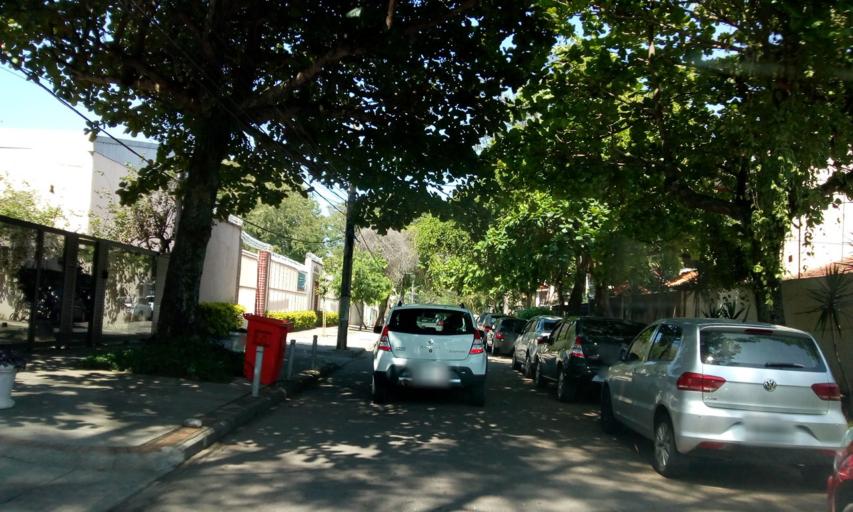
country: BR
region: Rio de Janeiro
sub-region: Nilopolis
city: Nilopolis
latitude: -23.0176
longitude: -43.4728
